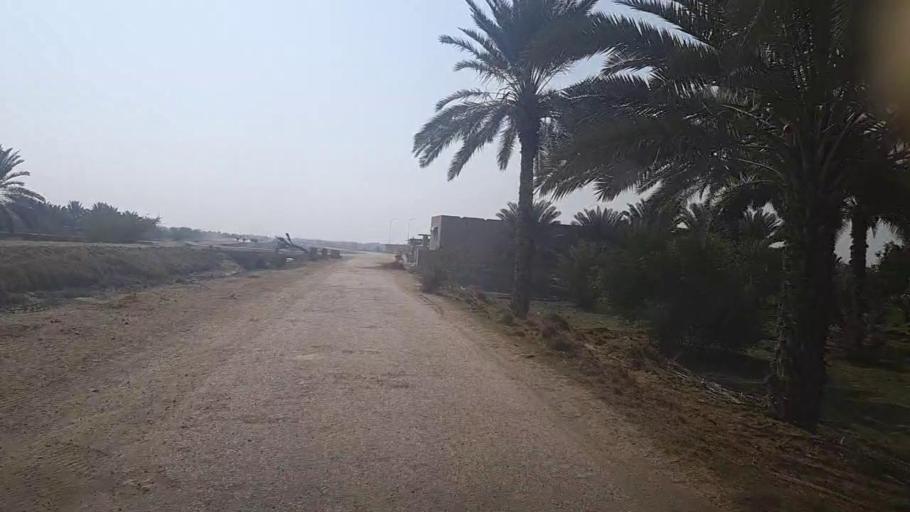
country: PK
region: Sindh
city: Khairpur
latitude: 27.4783
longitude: 68.8255
